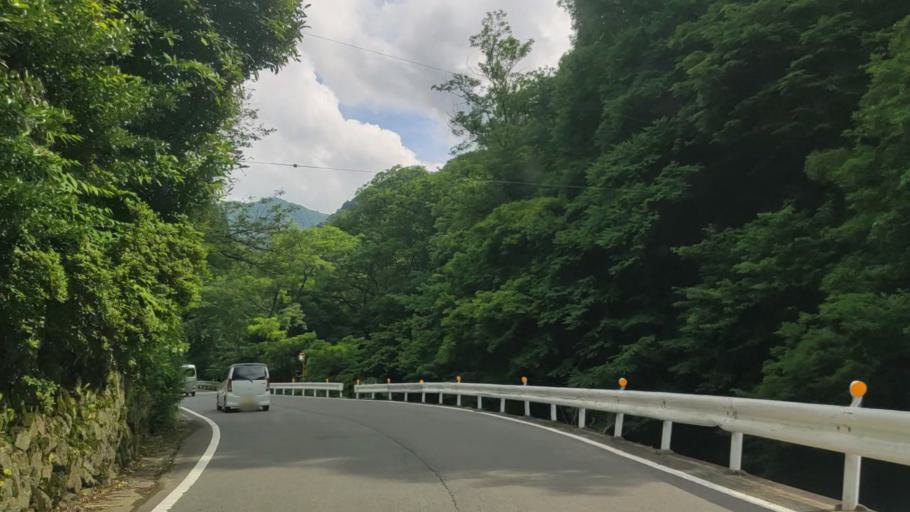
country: JP
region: Gunma
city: Tomioka
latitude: 36.0928
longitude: 138.7158
